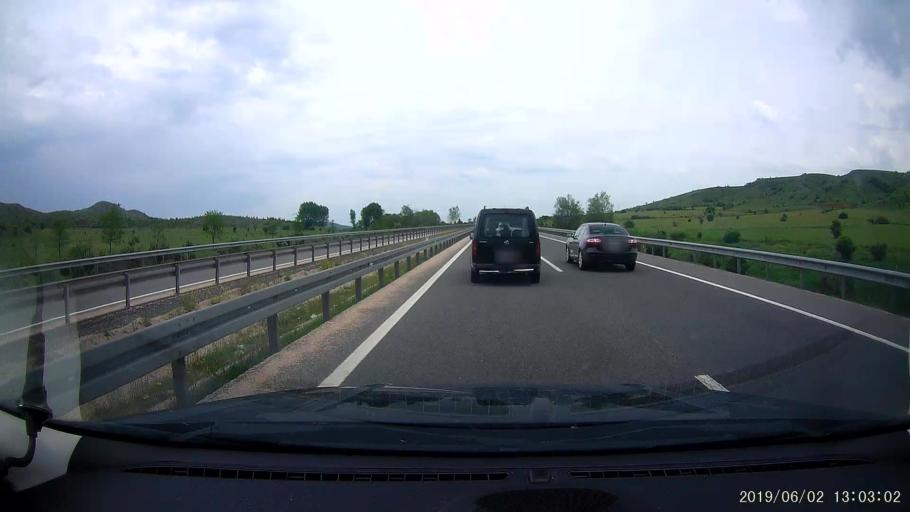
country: TR
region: Karabuk
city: Gozyeri
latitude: 40.8578
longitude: 32.4937
